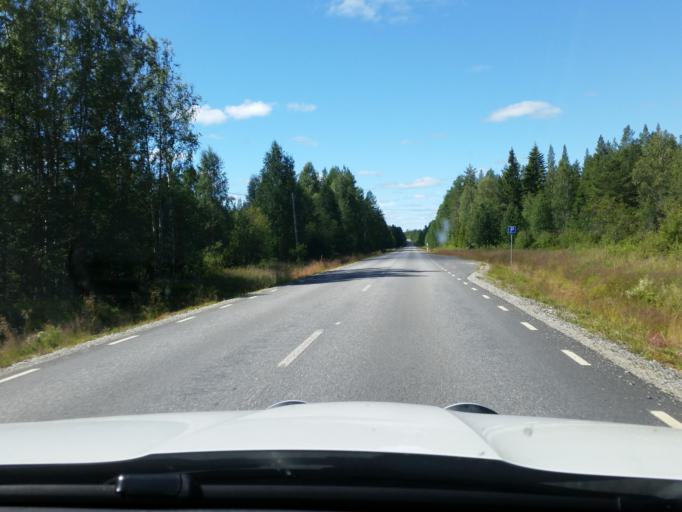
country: SE
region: Norrbotten
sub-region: Pitea Kommun
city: Roknas
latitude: 65.1976
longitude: 21.1236
